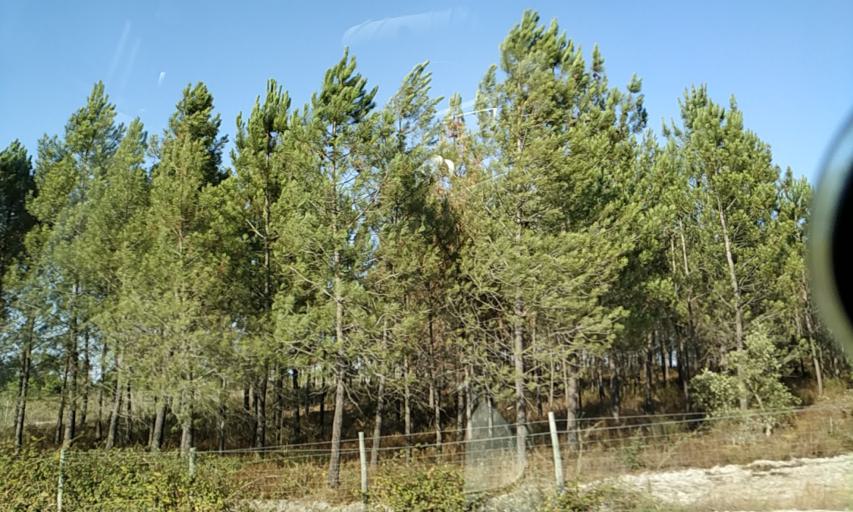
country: PT
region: Santarem
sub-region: Coruche
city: Coruche
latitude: 39.0359
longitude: -8.5602
